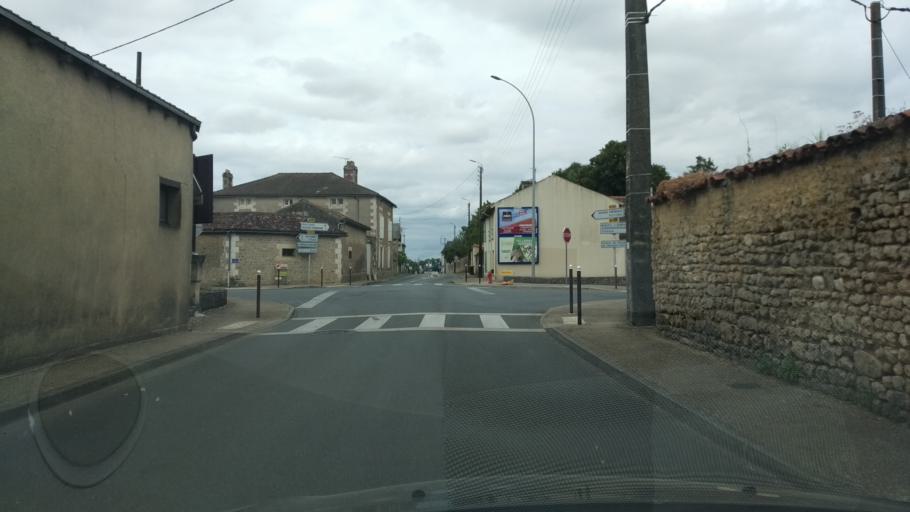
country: FR
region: Poitou-Charentes
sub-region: Departement de la Vienne
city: La Villedieu-du-Clain
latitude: 46.4577
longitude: 0.3671
